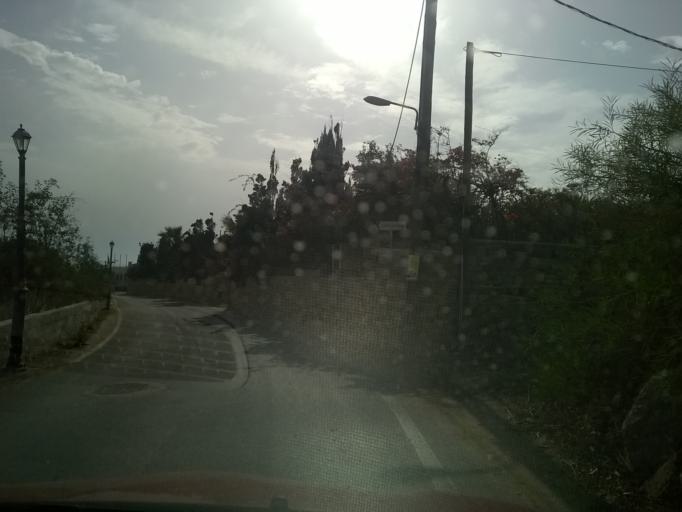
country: GR
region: South Aegean
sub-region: Nomos Kykladon
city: Naxos
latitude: 37.0833
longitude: 25.3477
